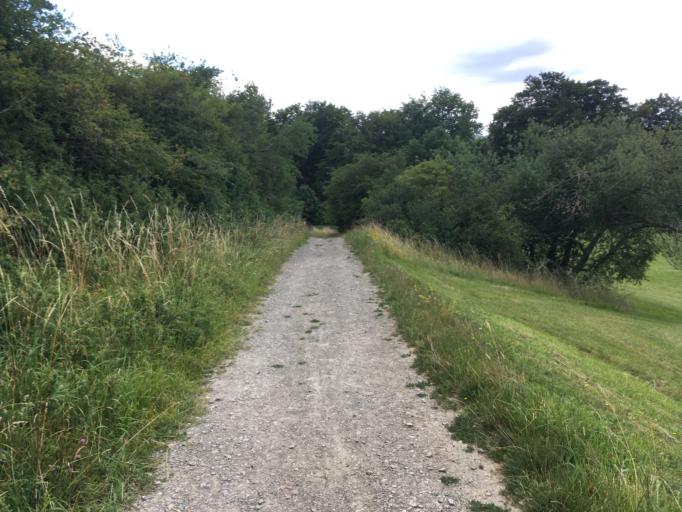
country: DE
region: Hesse
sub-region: Regierungsbezirk Kassel
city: Zierenberg
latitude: 51.3528
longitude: 9.3406
